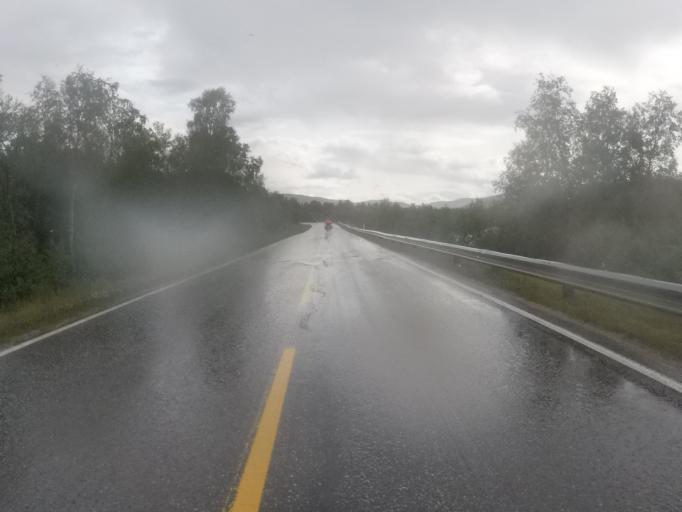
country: NO
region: Finnmark Fylke
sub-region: Porsanger
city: Lakselv
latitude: 69.8274
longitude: 25.1461
